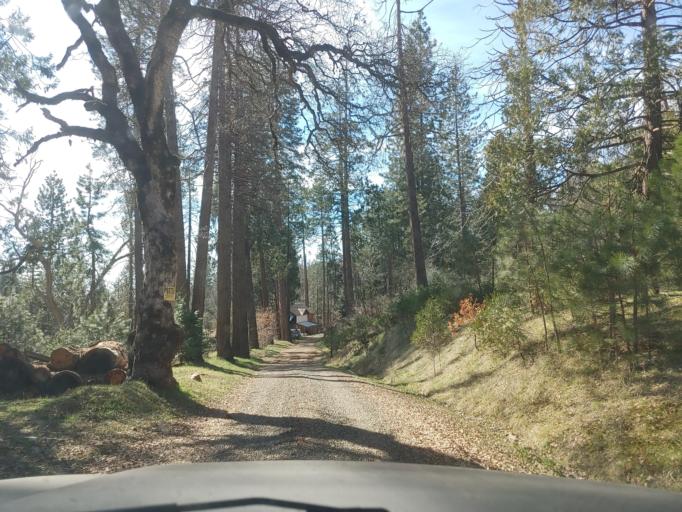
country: US
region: California
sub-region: Madera County
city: Ahwahnee
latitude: 37.4199
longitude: -119.6893
